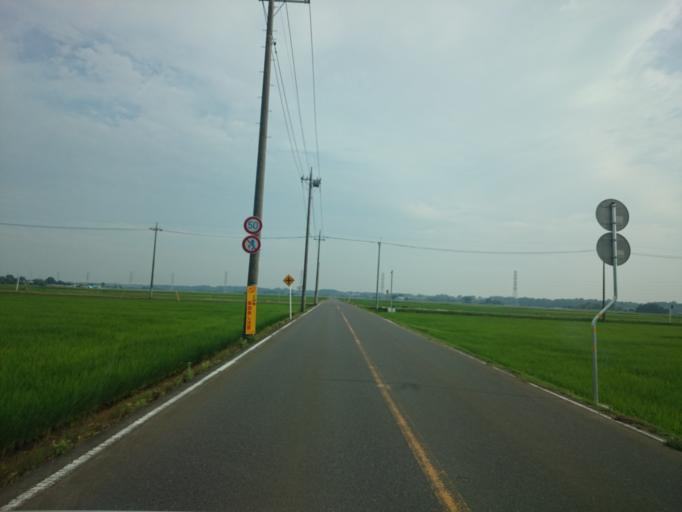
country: JP
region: Ibaraki
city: Tsukuba
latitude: 36.1641
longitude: 140.0989
